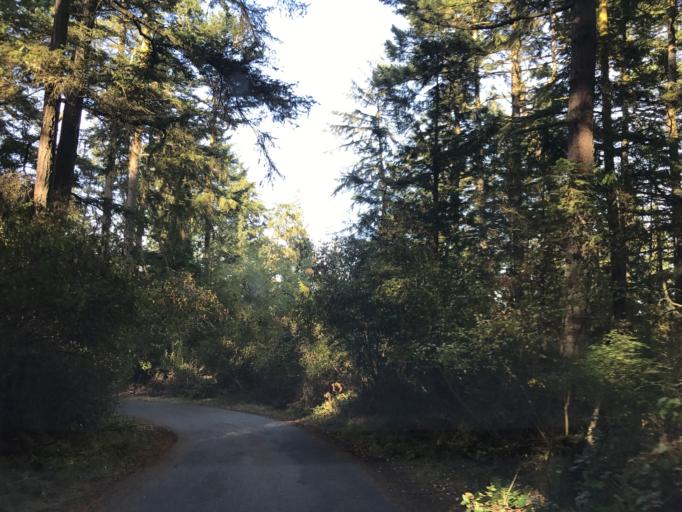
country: US
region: Washington
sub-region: Skagit County
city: Anacortes
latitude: 48.4933
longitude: -122.6907
